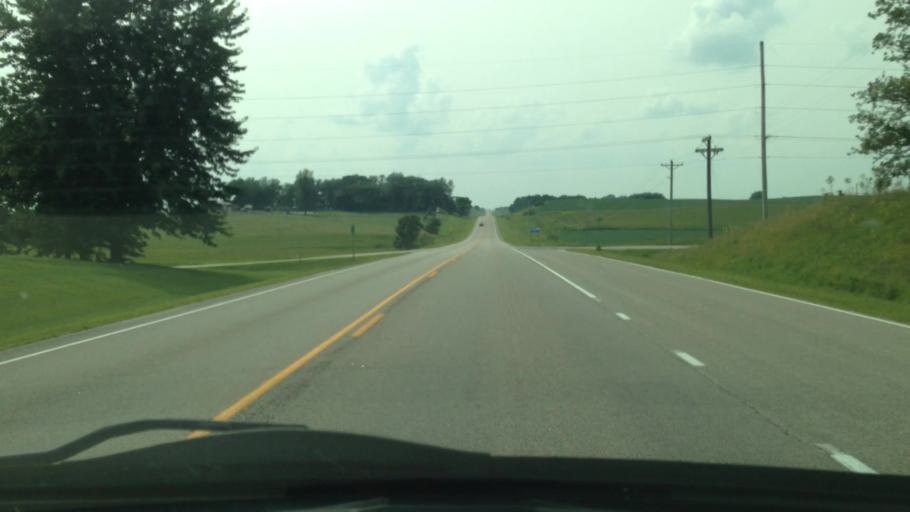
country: US
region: Minnesota
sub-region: Wabasha County
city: Plainview
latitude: 44.1654
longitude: -92.2179
